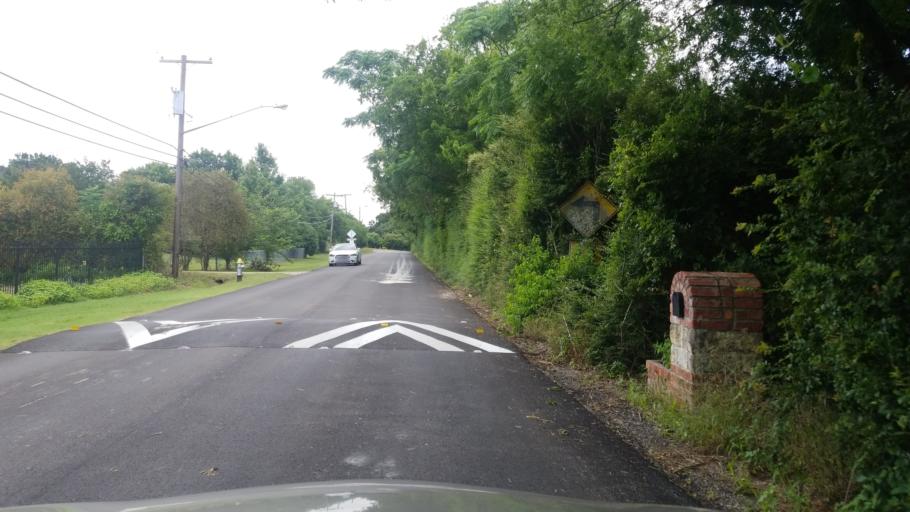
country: US
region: Texas
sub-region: Dallas County
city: Duncanville
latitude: 32.6780
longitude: -96.9341
